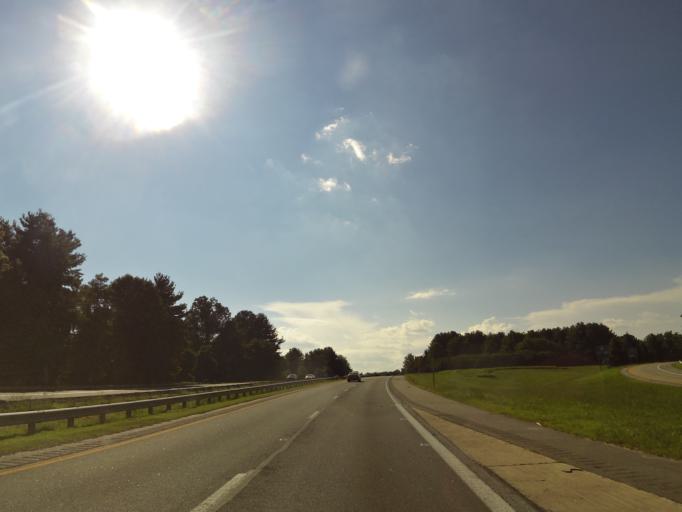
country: US
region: North Carolina
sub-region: Buncombe County
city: Biltmore Forest
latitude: 35.5579
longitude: -82.5350
